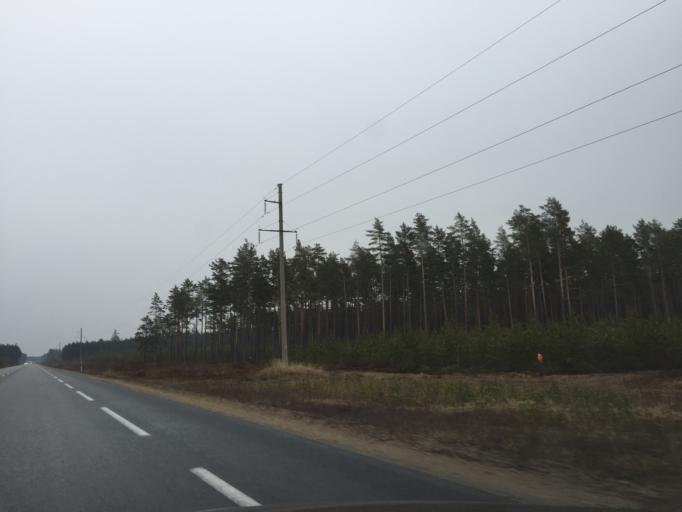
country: LV
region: Saulkrastu
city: Saulkrasti
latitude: 57.2121
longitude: 24.3940
